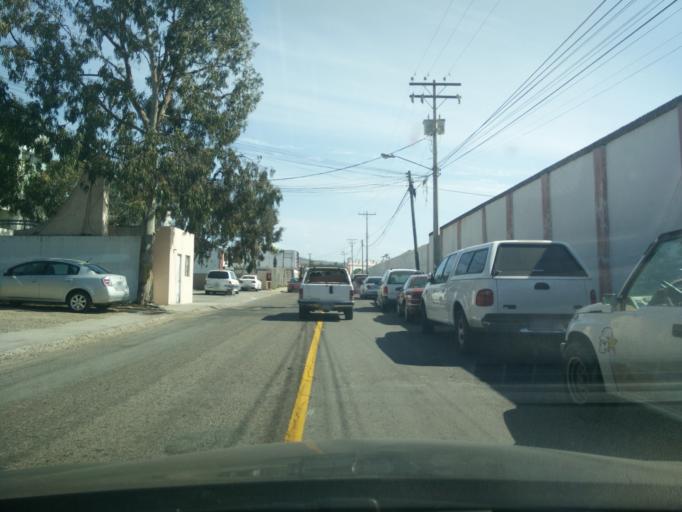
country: US
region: California
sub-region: San Diego County
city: Imperial Beach
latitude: 32.5332
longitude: -117.1203
